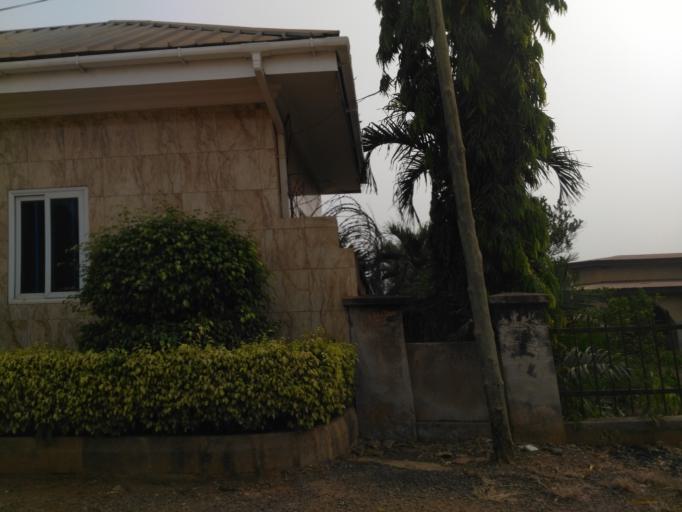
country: GH
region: Ashanti
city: Kumasi
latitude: 6.6535
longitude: -1.6249
